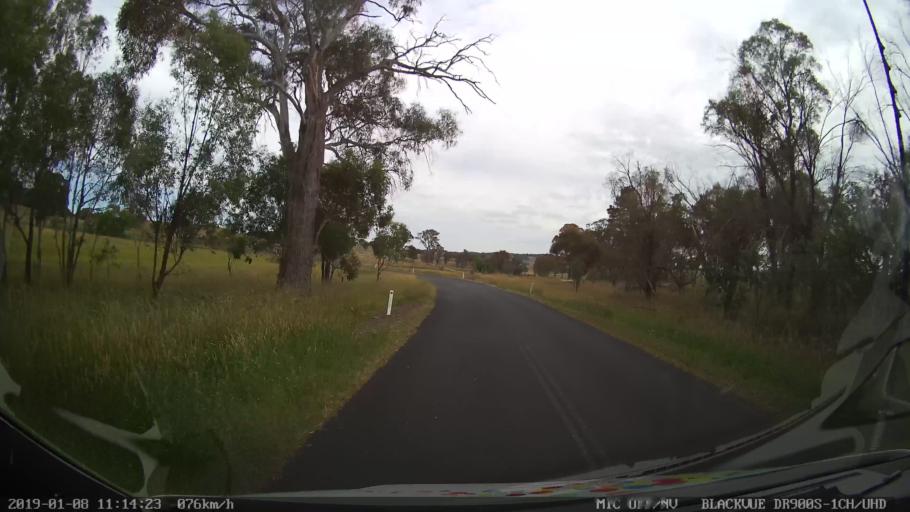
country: AU
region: New South Wales
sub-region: Guyra
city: Guyra
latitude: -30.2264
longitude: 151.5895
